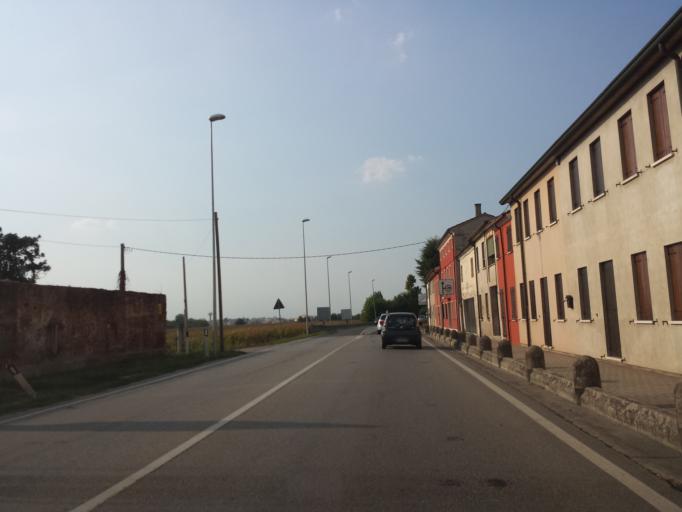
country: IT
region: Veneto
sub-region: Provincia di Padova
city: Arlesega
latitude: 45.4636
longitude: 11.7153
